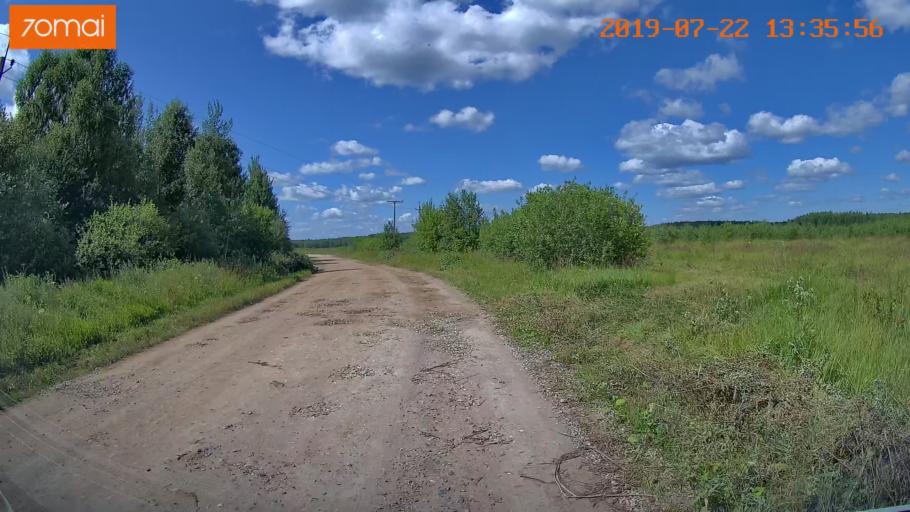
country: RU
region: Ivanovo
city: Novo-Talitsy
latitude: 57.0654
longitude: 40.8935
